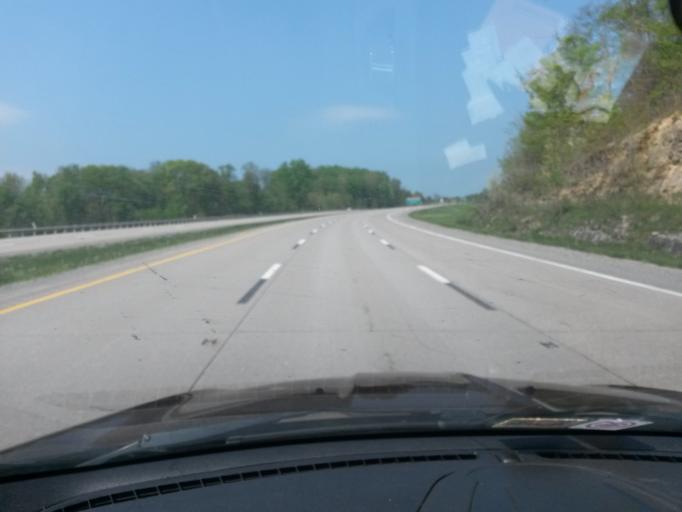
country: US
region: West Virginia
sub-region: Barbour County
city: Belington
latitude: 38.9616
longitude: -80.0291
